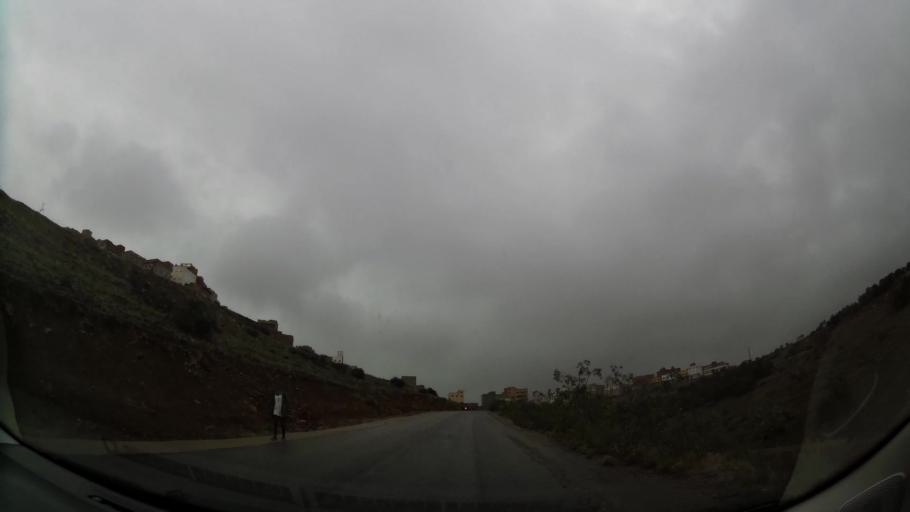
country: MA
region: Oriental
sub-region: Nador
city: Nador
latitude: 35.1870
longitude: -2.9354
